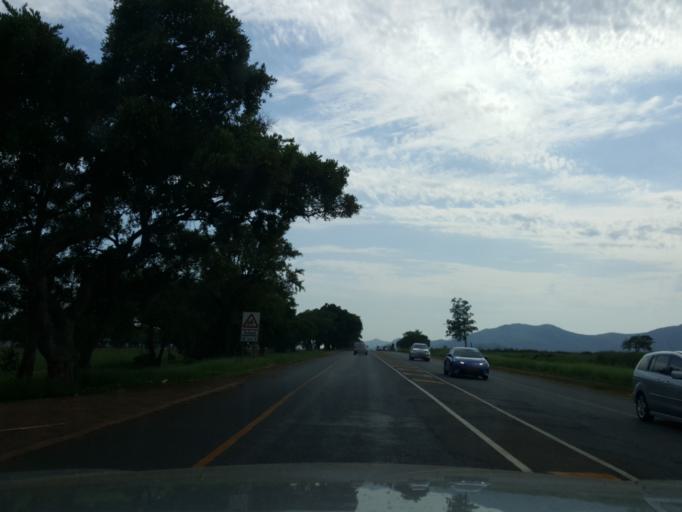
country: SZ
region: Hhohho
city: Ntfonjeni
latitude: -25.5063
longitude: 31.4900
